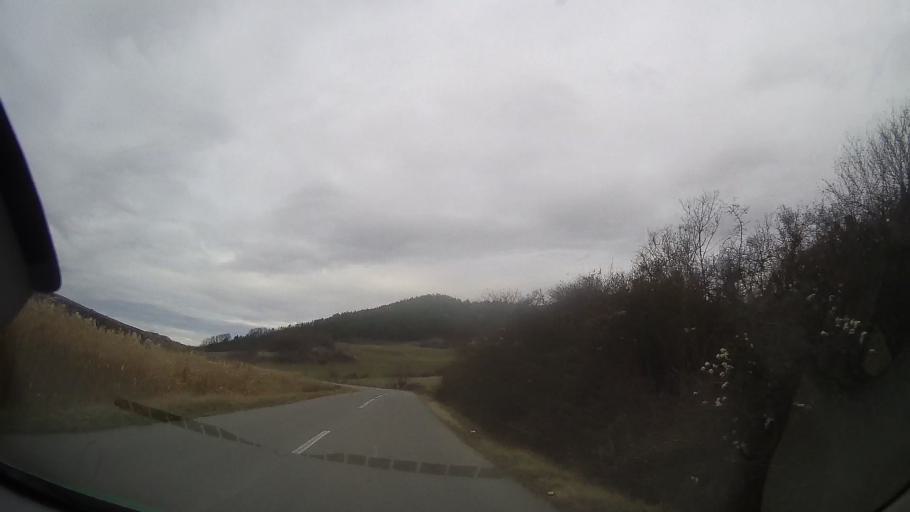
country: RO
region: Mures
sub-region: Comuna Bala
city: Bala
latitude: 46.7220
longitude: 24.5478
